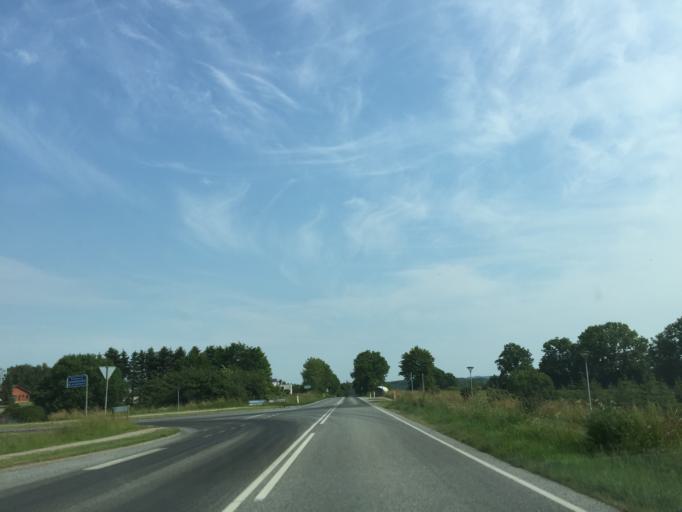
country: DK
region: Central Jutland
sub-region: Syddjurs Kommune
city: Ronde
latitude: 56.3089
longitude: 10.4442
